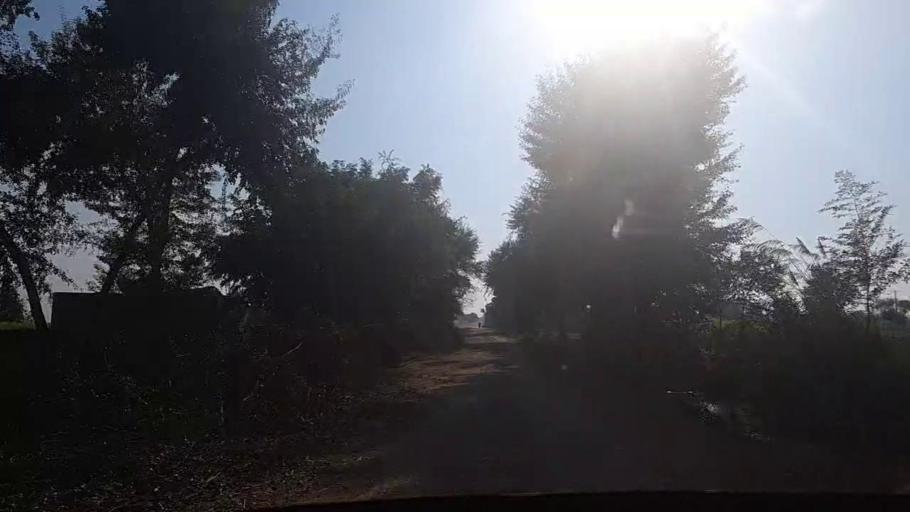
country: PK
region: Sindh
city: Gambat
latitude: 27.3746
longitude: 68.4659
